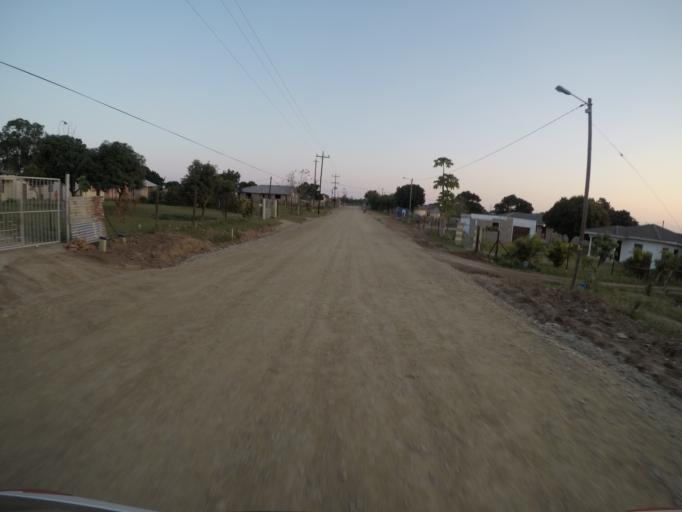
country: ZA
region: KwaZulu-Natal
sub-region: uThungulu District Municipality
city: Richards Bay
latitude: -28.7578
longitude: 32.1289
